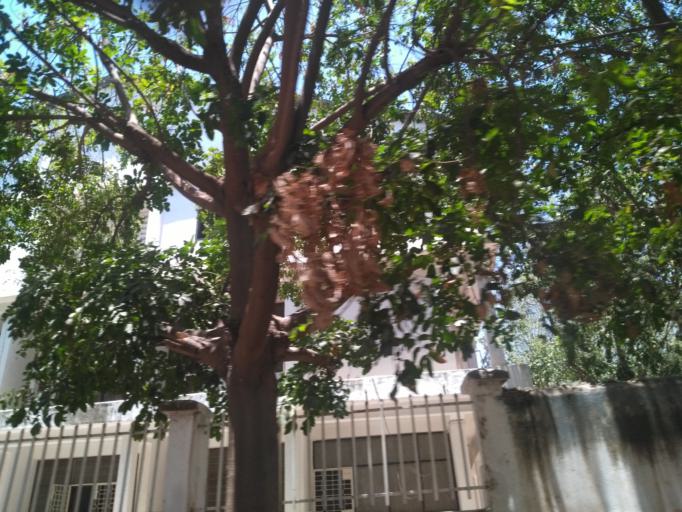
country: TZ
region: Dodoma
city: Dodoma
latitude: -6.1639
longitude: 35.7455
